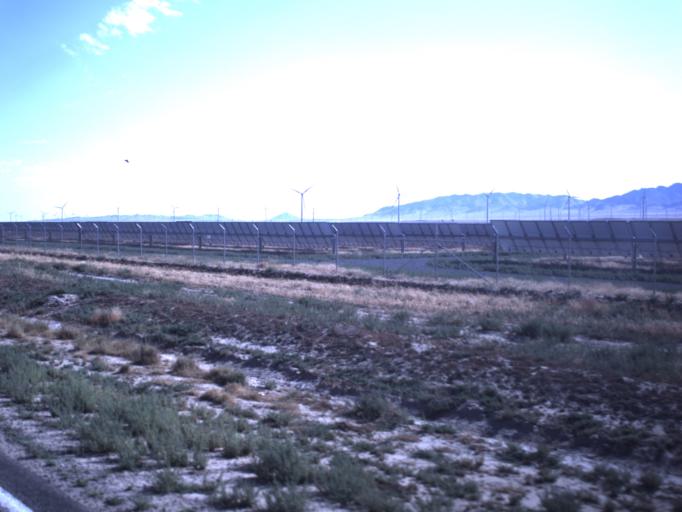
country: US
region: Utah
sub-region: Beaver County
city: Milford
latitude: 38.4904
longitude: -112.9911
